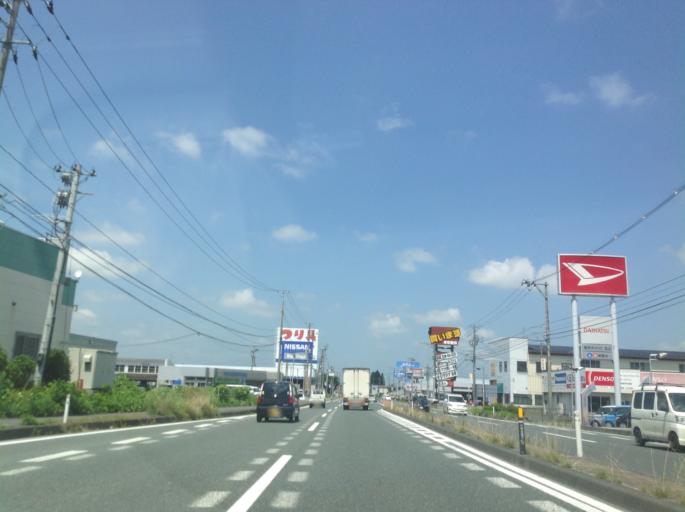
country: JP
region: Iwate
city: Kitakami
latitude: 39.3157
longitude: 141.1125
